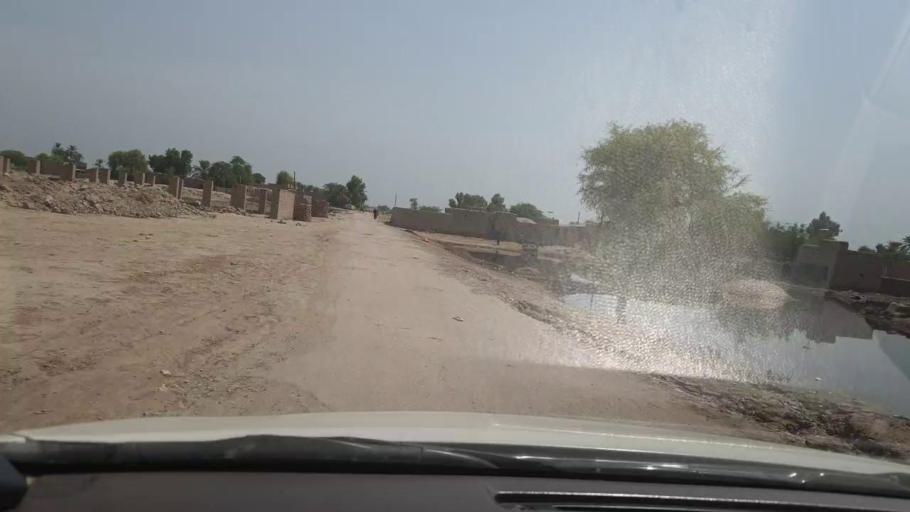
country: PK
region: Sindh
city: Shikarpur
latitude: 27.9442
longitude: 68.5975
